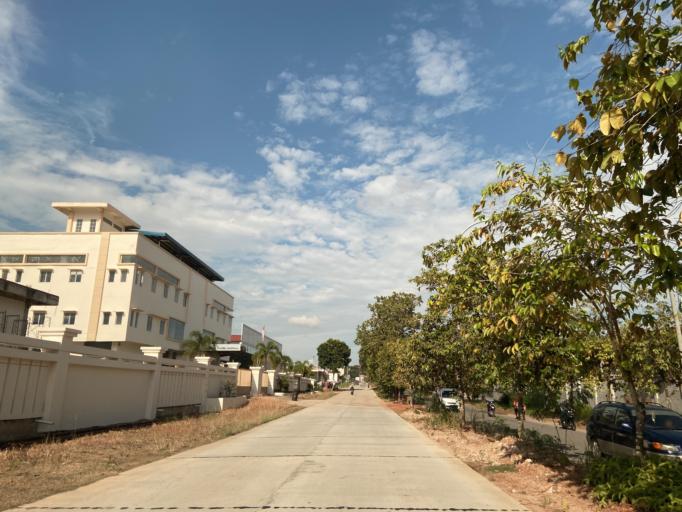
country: SG
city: Singapore
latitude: 1.1118
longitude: 104.0715
